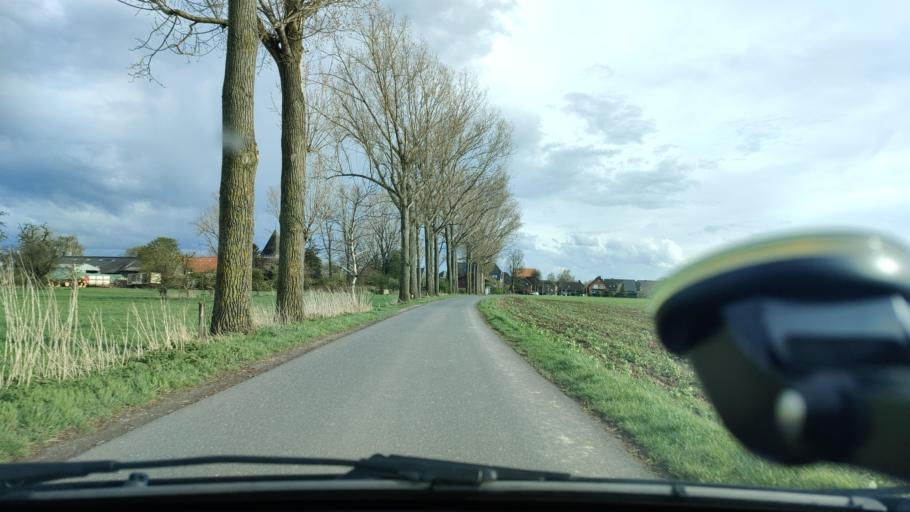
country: DE
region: North Rhine-Westphalia
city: Rees
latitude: 51.7353
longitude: 6.4106
